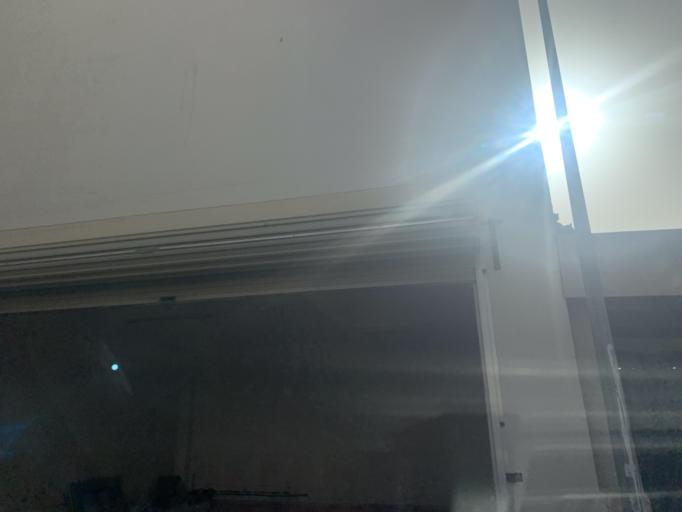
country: BH
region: Manama
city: Jidd Hafs
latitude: 26.2278
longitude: 50.5473
